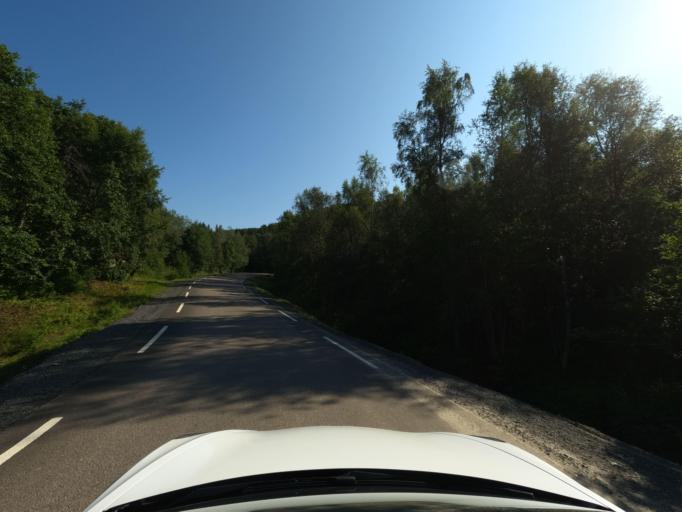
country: NO
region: Nordland
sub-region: Narvik
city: Narvik
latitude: 68.3946
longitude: 17.3016
